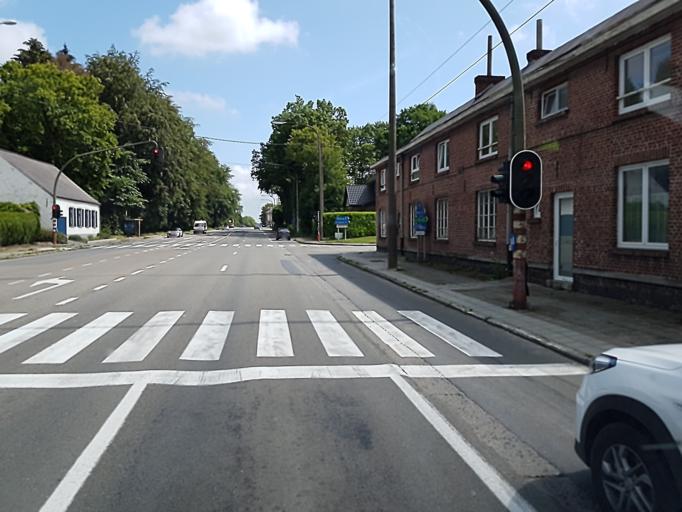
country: BE
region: Wallonia
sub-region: Province du Hainaut
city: Mons
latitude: 50.5034
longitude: 3.9950
